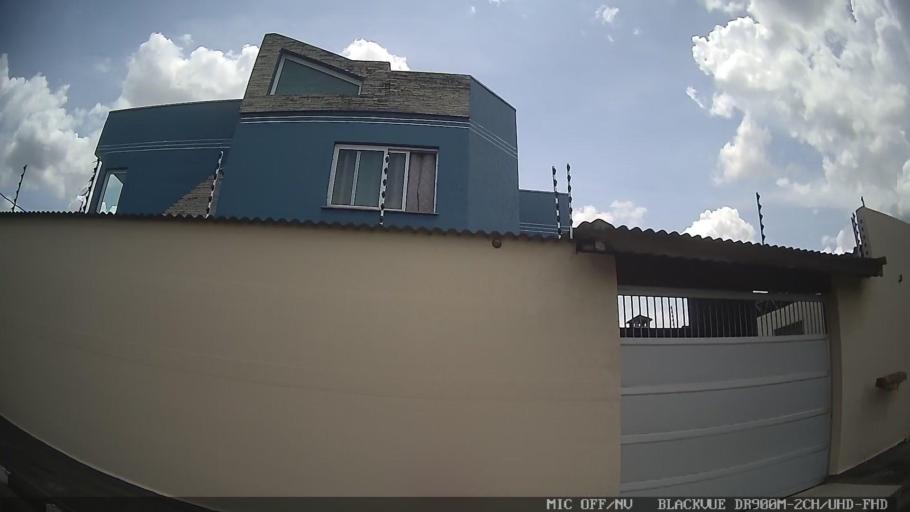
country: BR
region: Sao Paulo
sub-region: Suzano
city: Suzano
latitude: -23.5328
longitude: -46.3182
